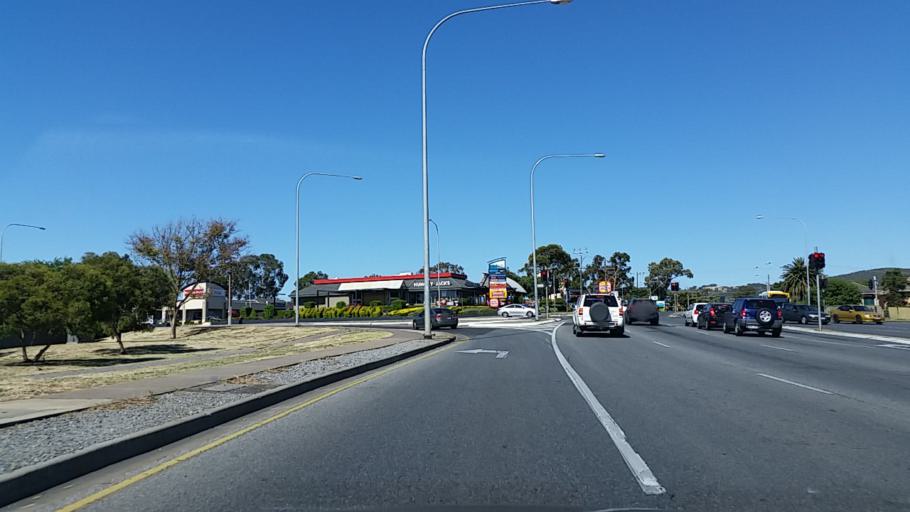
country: AU
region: South Australia
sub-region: Tea Tree Gully
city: Hope Valley
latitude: -34.8280
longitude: 138.6930
